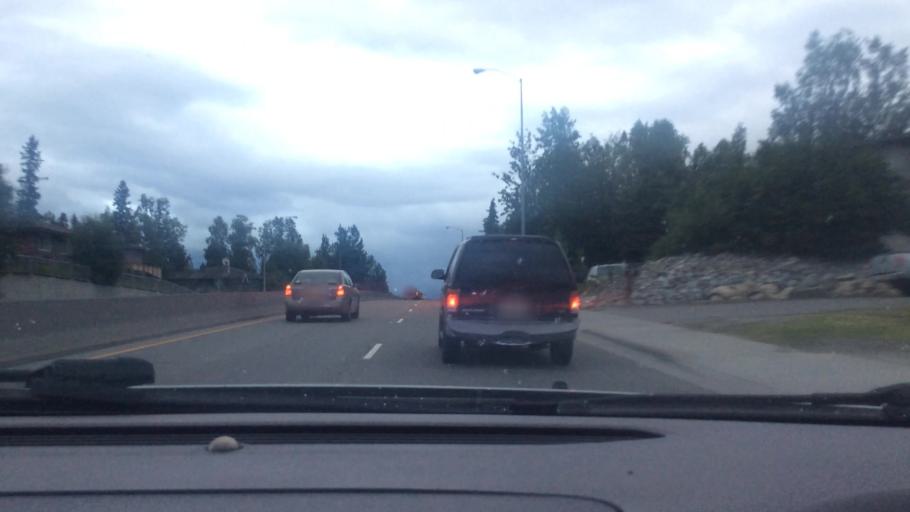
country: US
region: Alaska
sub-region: Anchorage Municipality
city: Anchorage
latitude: 61.1873
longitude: -149.7784
